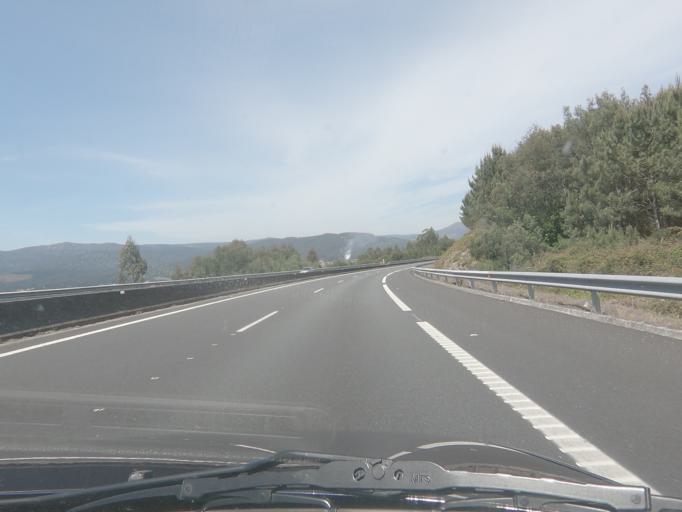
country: ES
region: Galicia
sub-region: Provincia de Pontevedra
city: Valga
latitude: 42.7068
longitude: -8.6426
